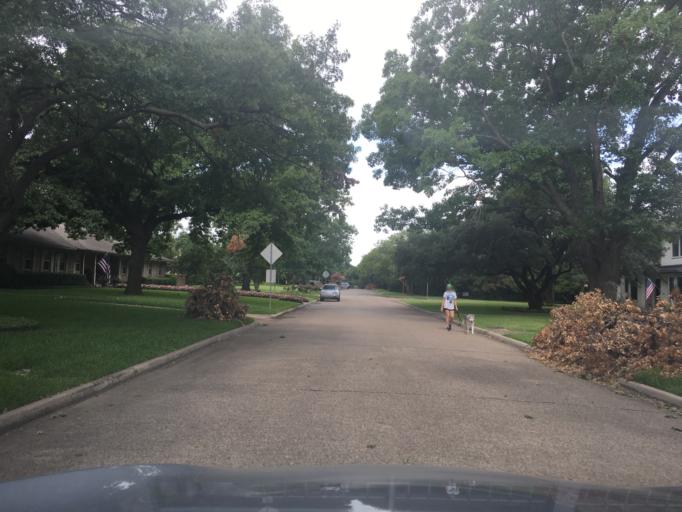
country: US
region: Texas
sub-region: Dallas County
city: Addison
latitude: 32.9110
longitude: -96.8332
